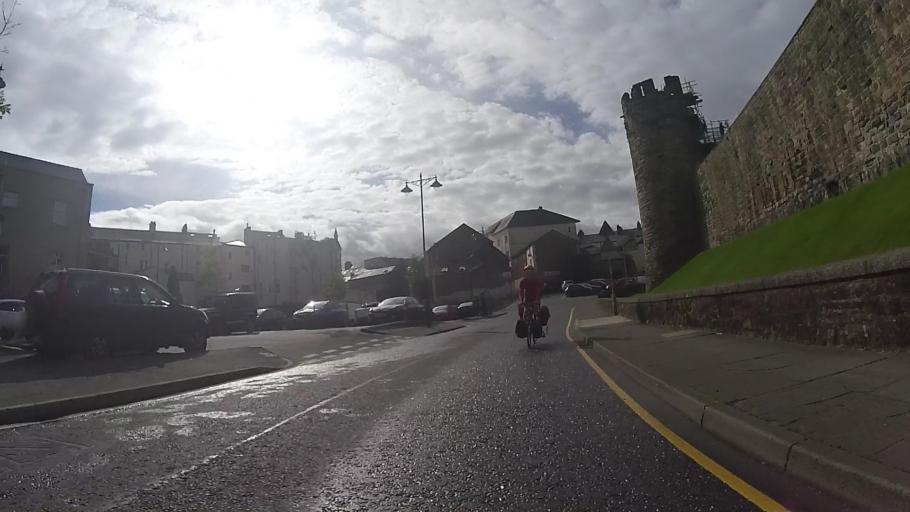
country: GB
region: Wales
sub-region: Gwynedd
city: Caernarfon
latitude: 53.1407
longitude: -4.2751
